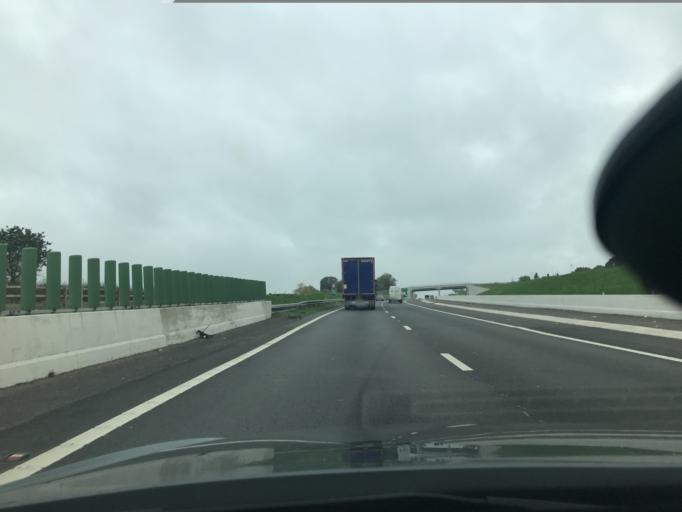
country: GB
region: England
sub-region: Cheshire East
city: Mere
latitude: 53.3581
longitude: -2.3966
